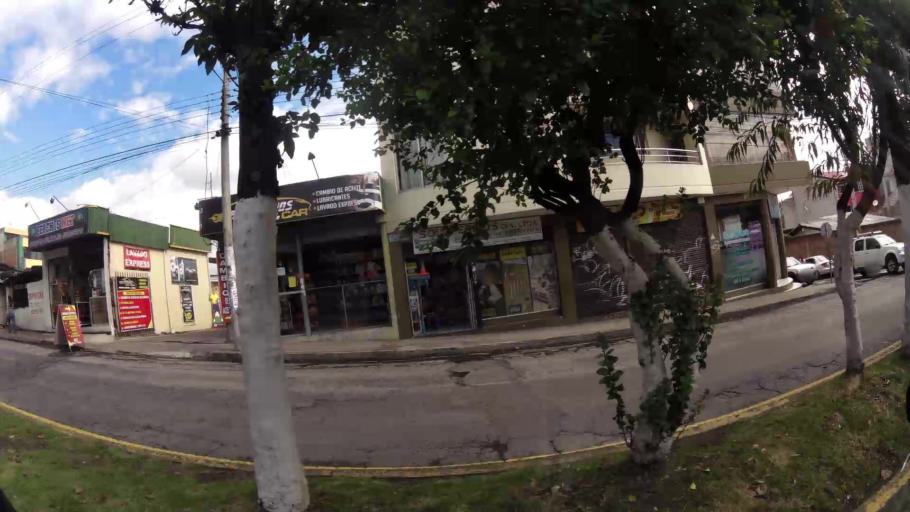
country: EC
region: Pichincha
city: Sangolqui
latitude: -0.3317
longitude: -78.4475
